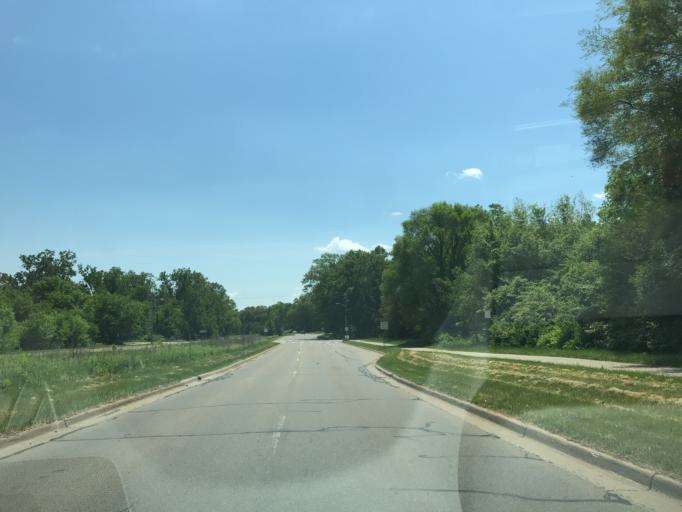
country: US
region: Michigan
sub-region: Washtenaw County
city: Ann Arbor
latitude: 42.2891
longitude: -83.7041
